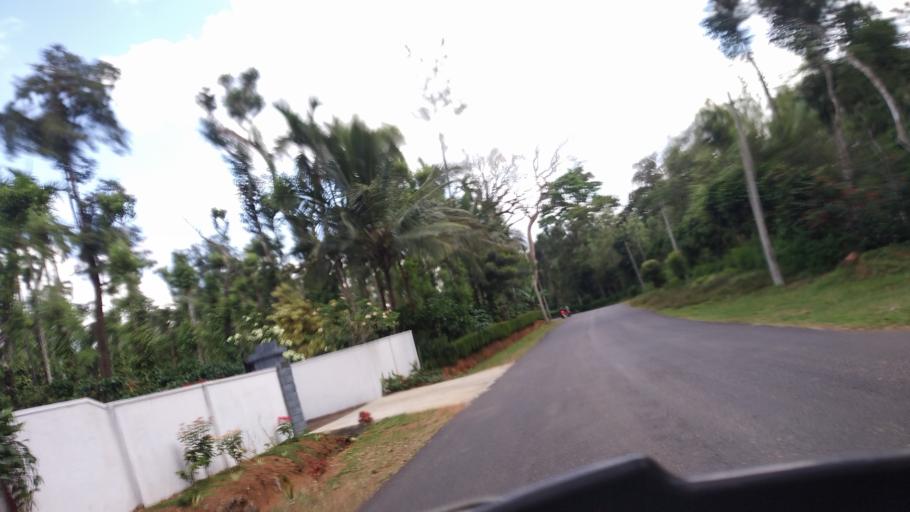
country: IN
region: Karnataka
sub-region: Kodagu
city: Ponnampet
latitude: 12.0339
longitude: 75.9273
